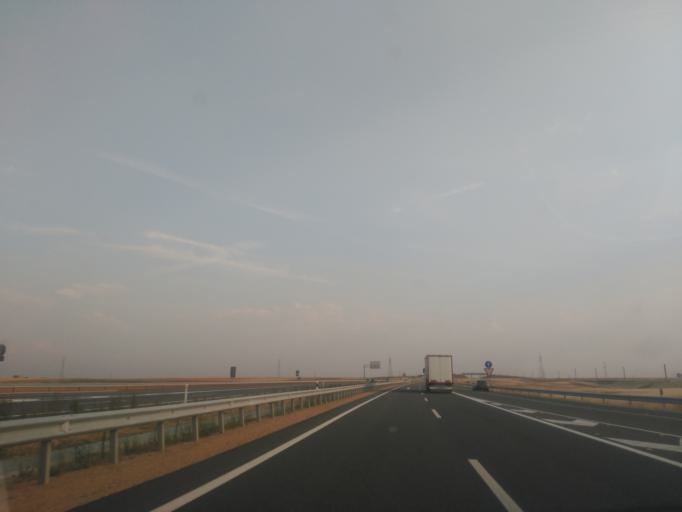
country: ES
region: Castille and Leon
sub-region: Provincia de Zamora
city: Montamarta
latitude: 41.6309
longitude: -5.7891
